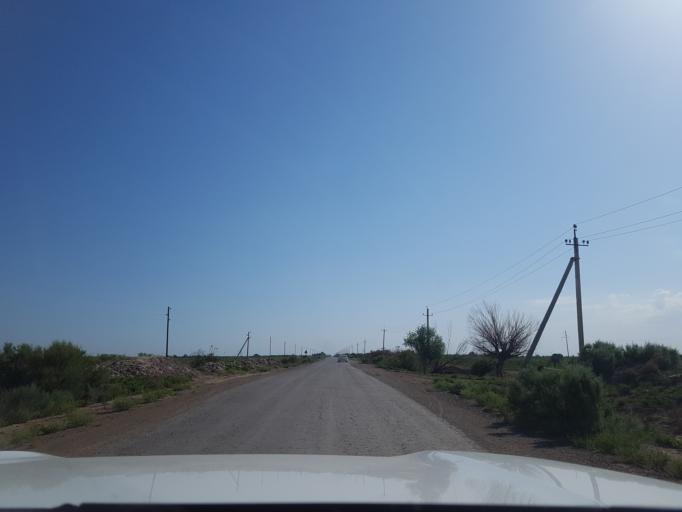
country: TM
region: Dasoguz
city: Koeneuergench
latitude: 42.0880
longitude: 58.8845
